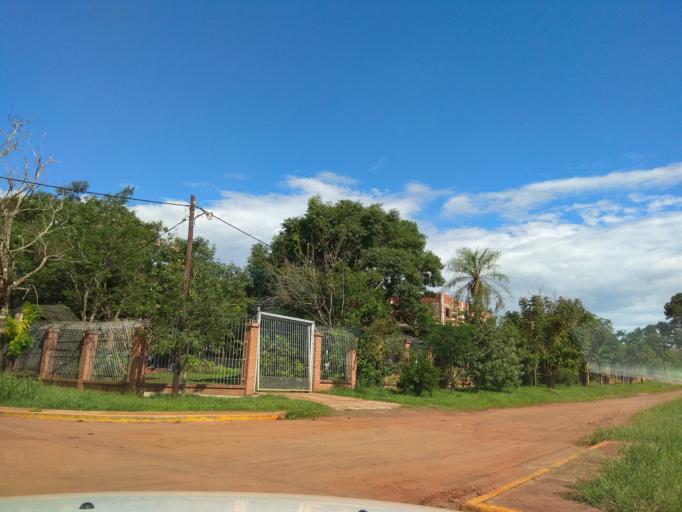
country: AR
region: Misiones
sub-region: Departamento de Candelaria
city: Candelaria
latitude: -27.4518
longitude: -55.7540
